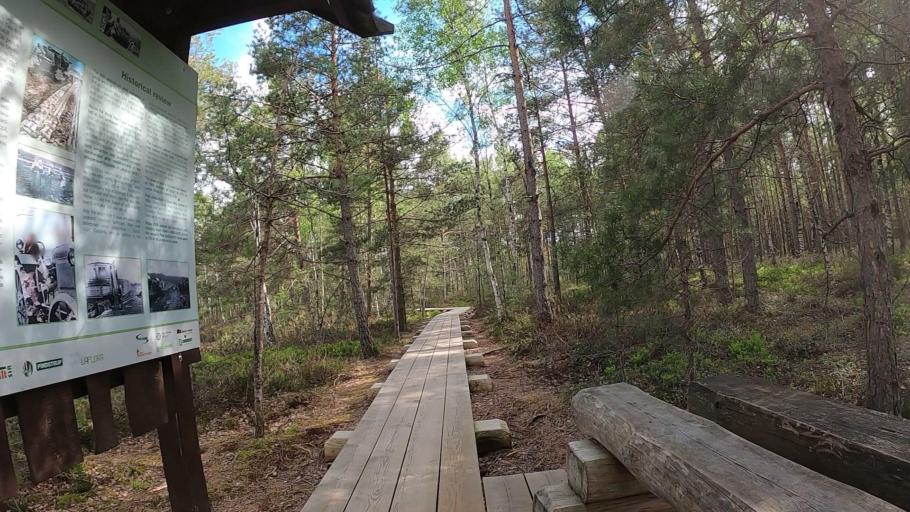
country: LV
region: Jurmala
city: Jurmala
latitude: 56.8602
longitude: 23.7949
